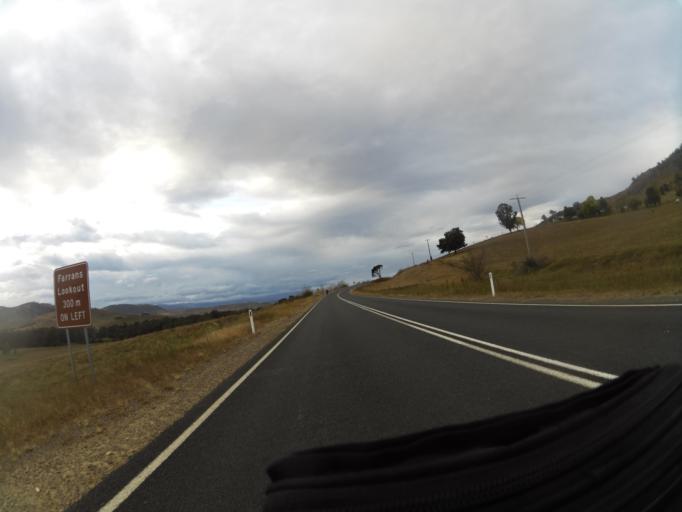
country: AU
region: New South Wales
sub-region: Snowy River
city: Jindabyne
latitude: -36.0830
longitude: 147.9770
